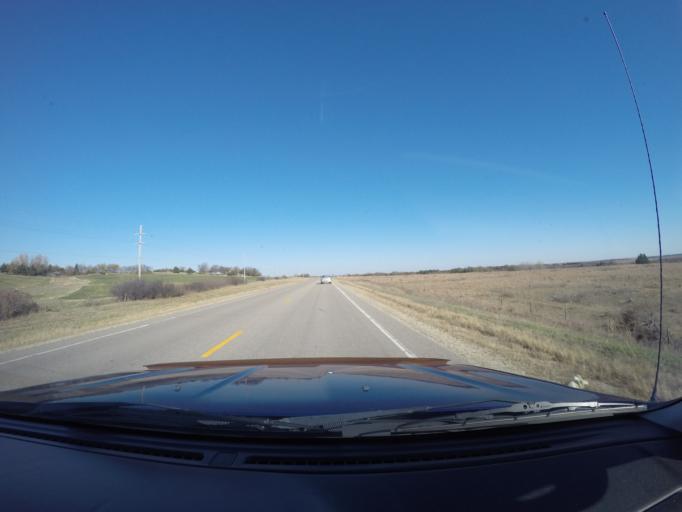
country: US
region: Kansas
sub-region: Riley County
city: Ogden
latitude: 39.3604
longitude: -96.7563
